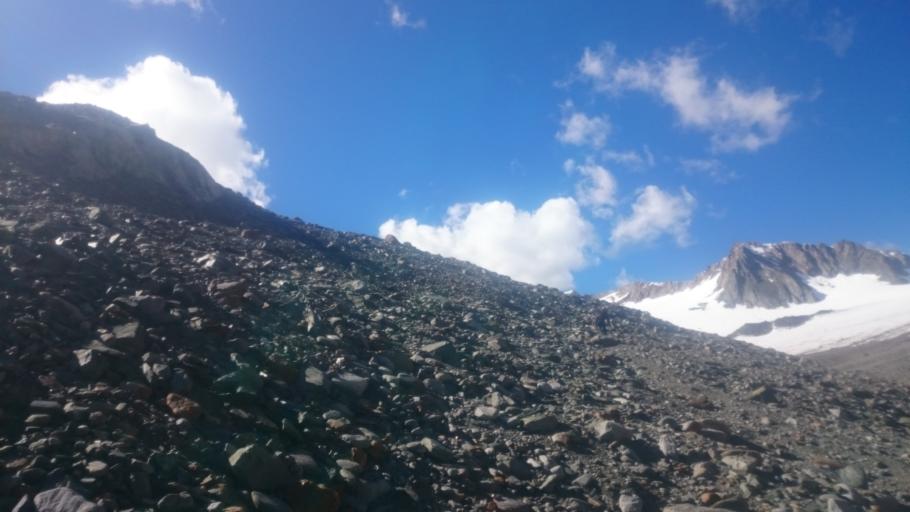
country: IT
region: Trentino-Alto Adige
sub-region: Bolzano
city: Senales
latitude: 46.8673
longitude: 10.8270
